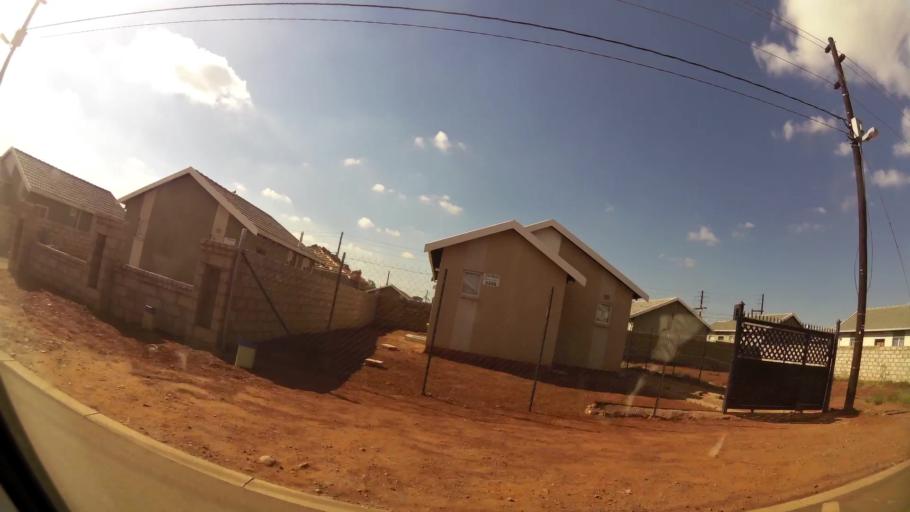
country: ZA
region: Gauteng
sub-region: City of Tshwane Metropolitan Municipality
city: Cullinan
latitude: -25.6846
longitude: 28.4097
